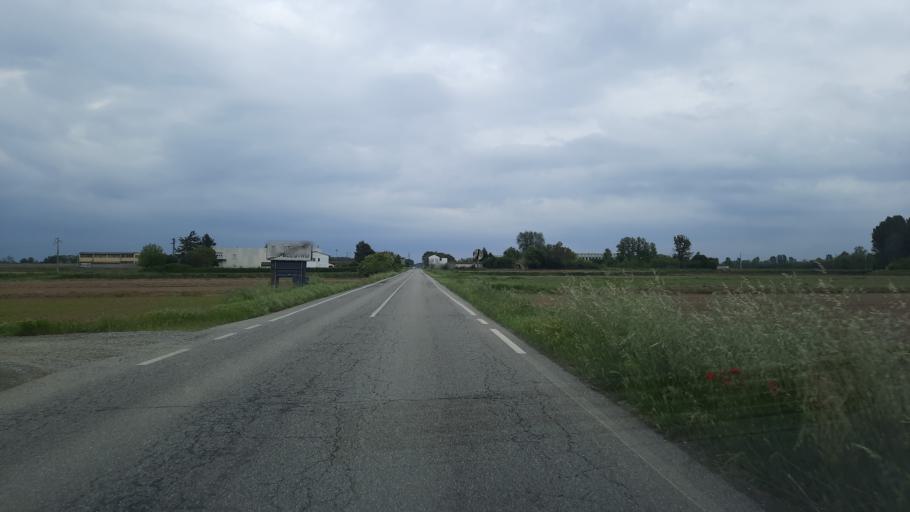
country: IT
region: Lombardy
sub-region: Provincia di Pavia
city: Palestro
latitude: 45.2980
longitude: 8.5450
